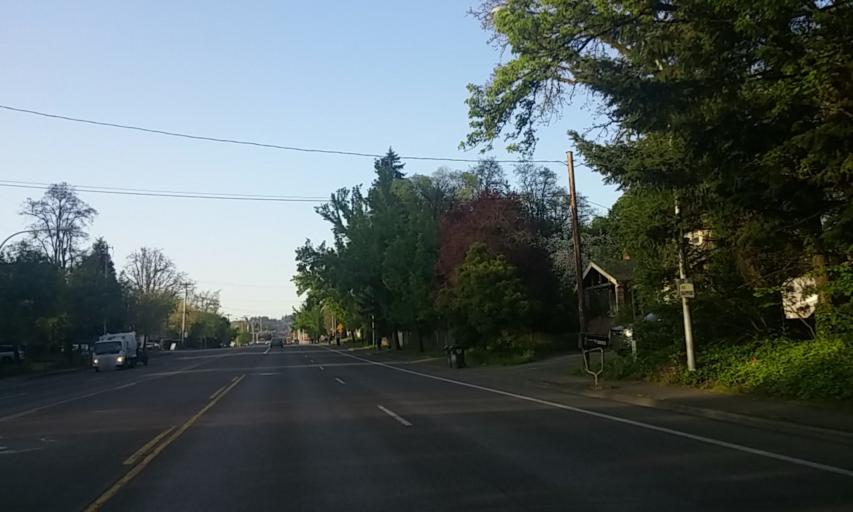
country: US
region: Oregon
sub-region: Washington County
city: Aloha
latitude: 45.4978
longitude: -122.8673
